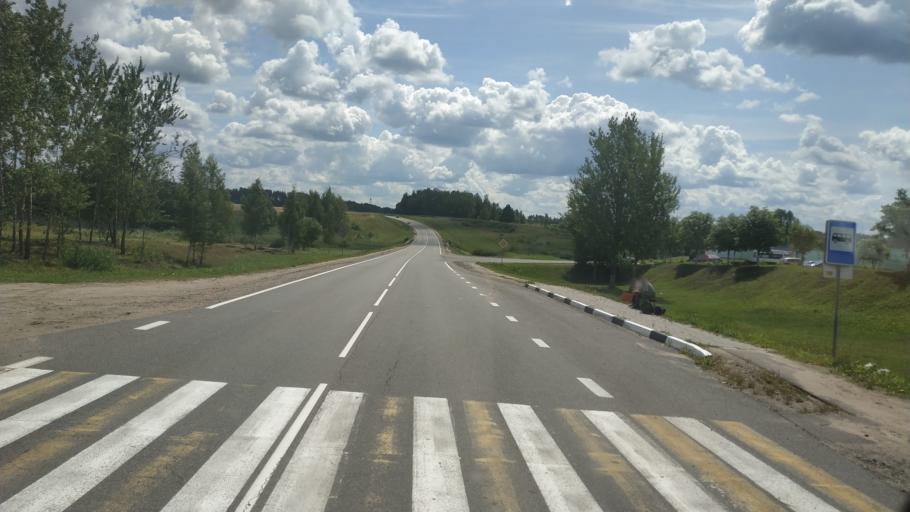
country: BY
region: Mogilev
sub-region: Mahilyowski Rayon
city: Veyno
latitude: 53.8371
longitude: 30.3988
